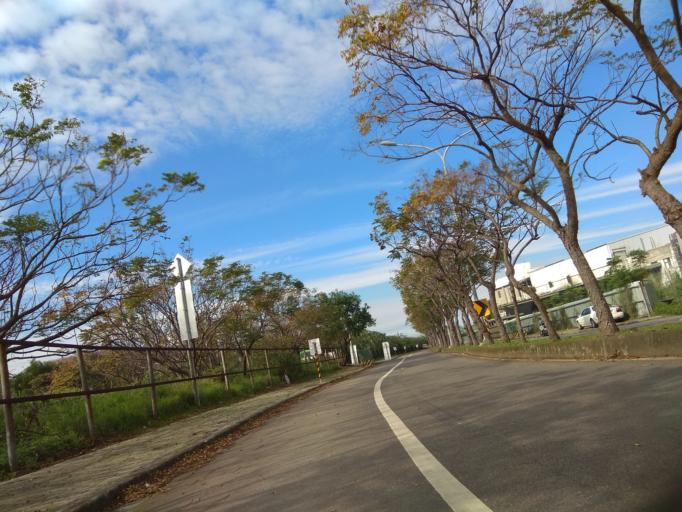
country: TW
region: Taiwan
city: Taoyuan City
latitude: 25.0563
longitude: 121.1804
